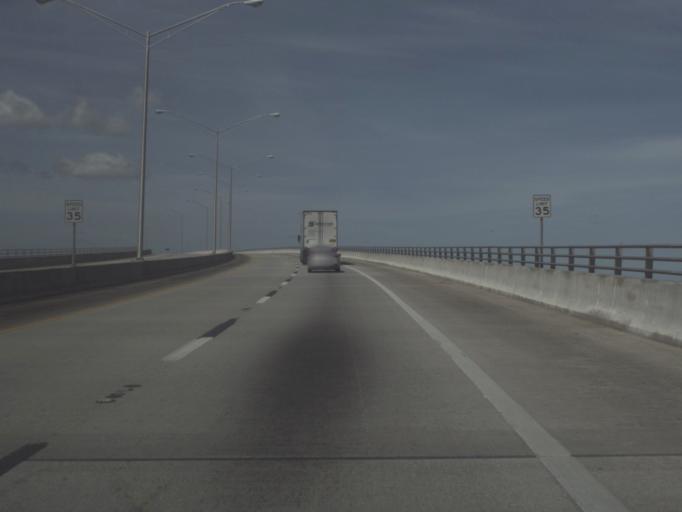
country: US
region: Florida
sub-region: Glades County
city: Moore Haven
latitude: 26.8319
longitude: -81.0854
